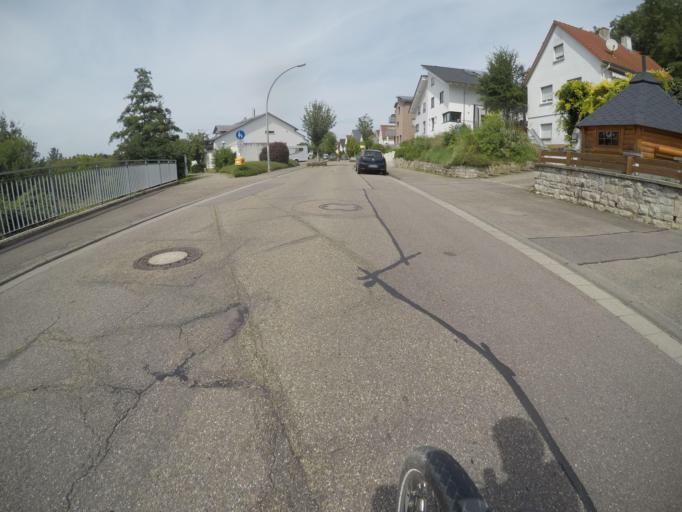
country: DE
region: Baden-Wuerttemberg
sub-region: Karlsruhe Region
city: Bruchsal
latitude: 49.1191
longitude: 8.6154
